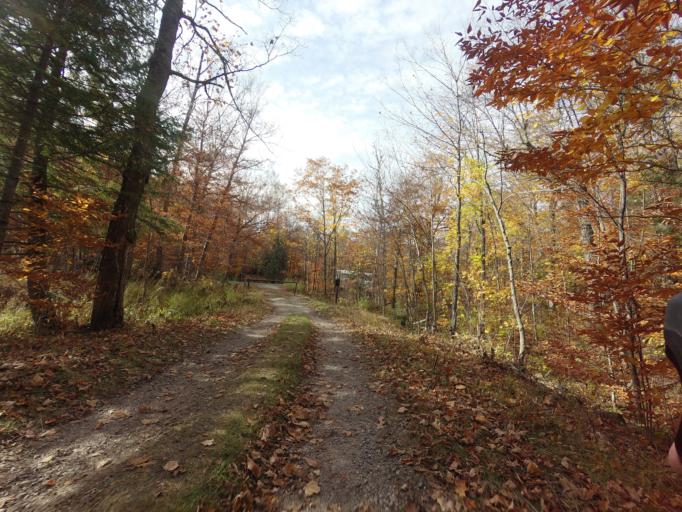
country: CA
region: Quebec
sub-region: Outaouais
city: Wakefield
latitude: 45.5061
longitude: -75.8798
